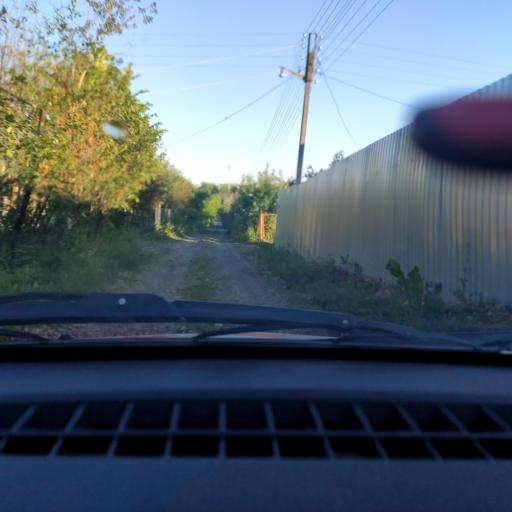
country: RU
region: Bashkortostan
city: Karmaskaly
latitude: 54.3680
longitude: 55.9031
